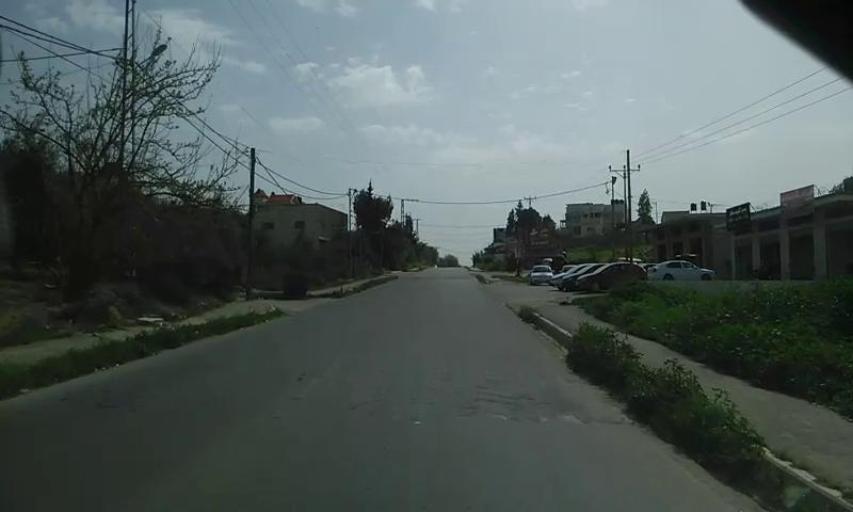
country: PS
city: Bir al Basha
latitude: 32.4210
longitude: 35.2311
